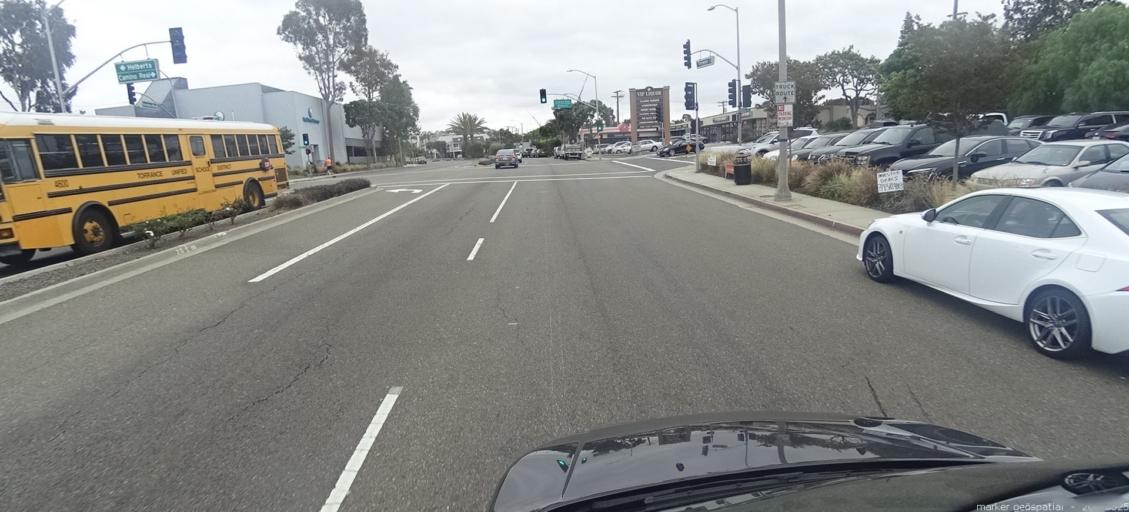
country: US
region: California
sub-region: Los Angeles County
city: Redondo Beach
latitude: 33.8377
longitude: -118.3824
